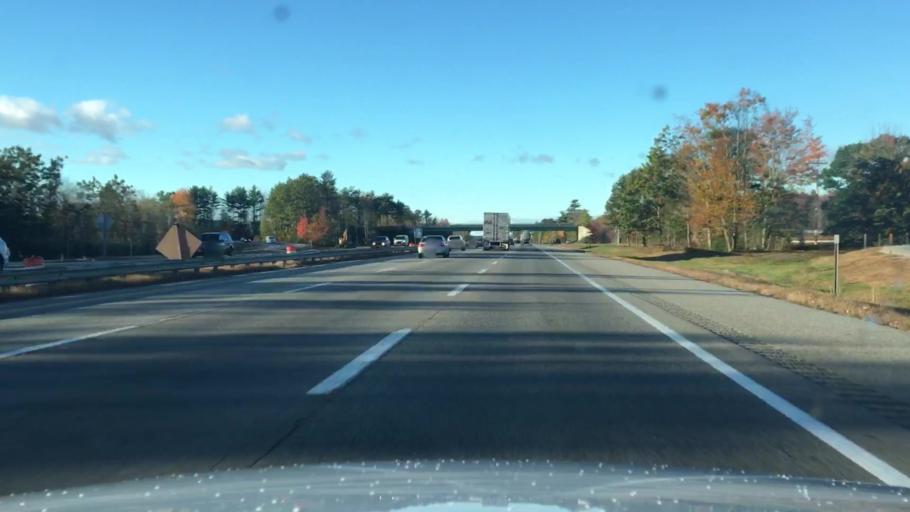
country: US
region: Maine
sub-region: Cumberland County
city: West Scarborough
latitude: 43.6077
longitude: -70.3699
